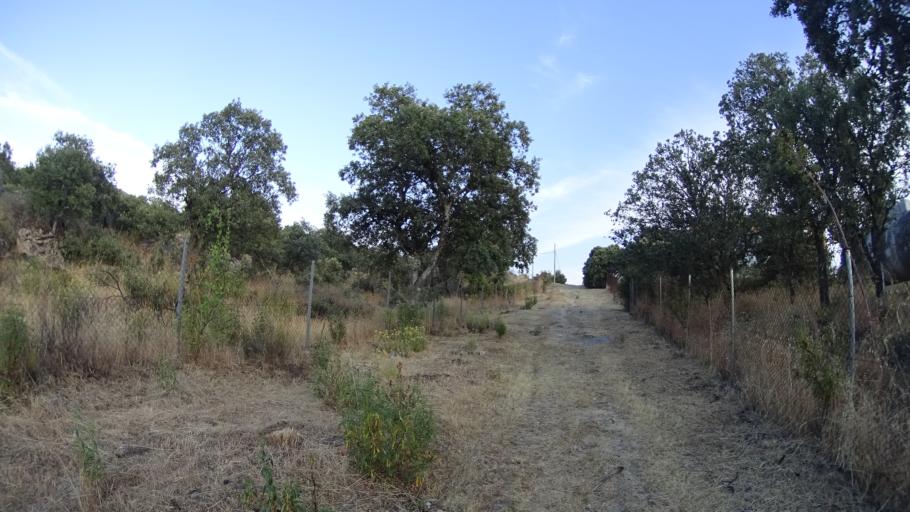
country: ES
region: Madrid
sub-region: Provincia de Madrid
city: Torrelodones
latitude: 40.5904
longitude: -3.9454
